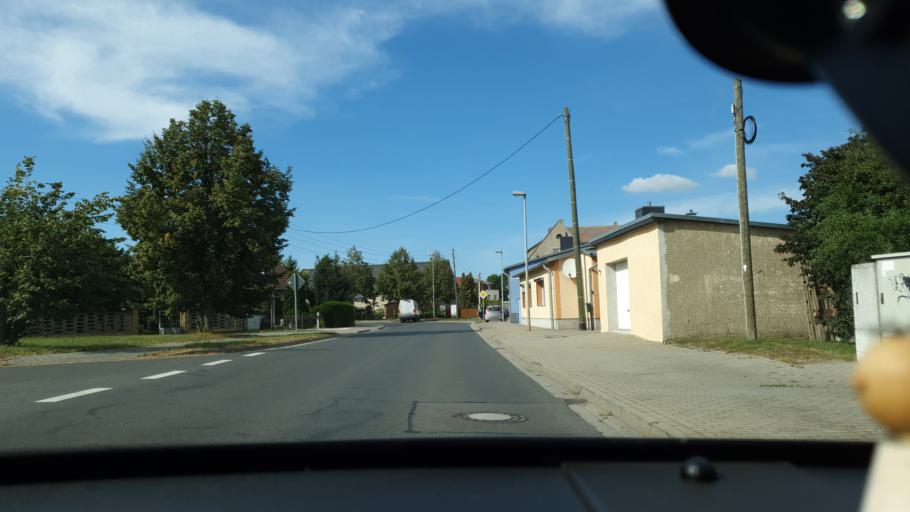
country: DE
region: Saxony
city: Krostitz
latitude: 51.4572
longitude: 12.4560
